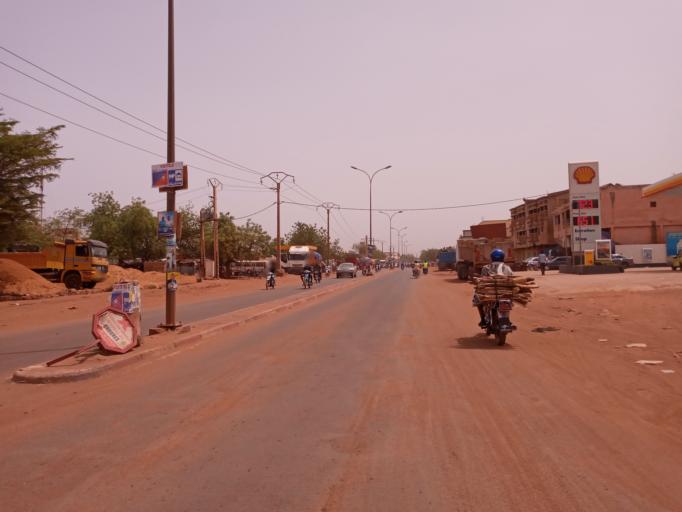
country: ML
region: Bamako
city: Bamako
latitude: 12.6683
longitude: -7.9266
